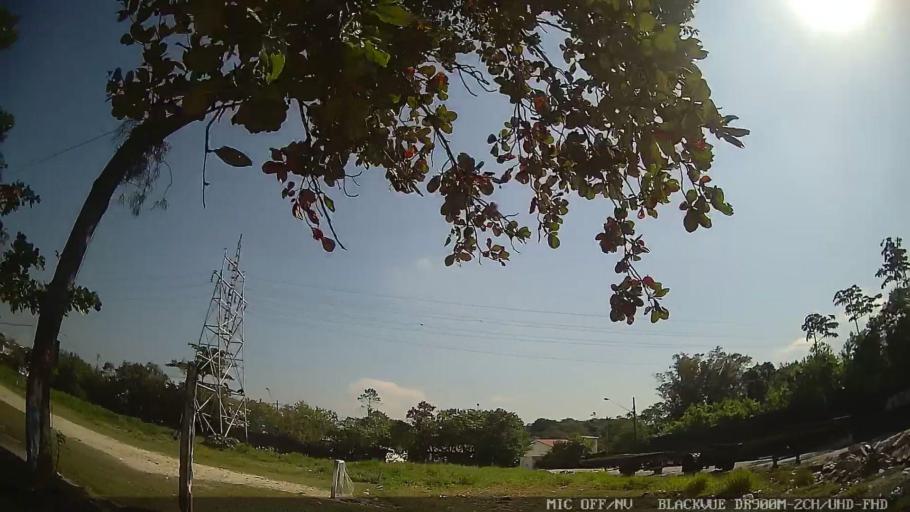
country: BR
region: Sao Paulo
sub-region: Santos
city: Santos
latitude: -23.9393
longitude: -46.2966
